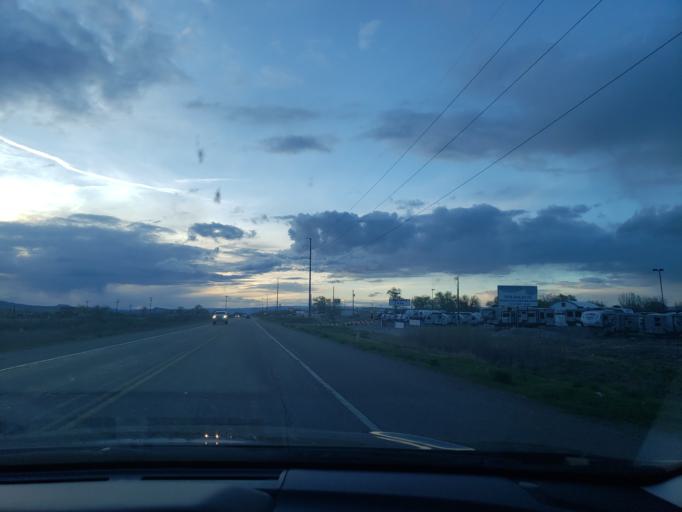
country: US
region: Colorado
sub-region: Mesa County
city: Redlands
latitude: 39.1178
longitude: -108.6598
